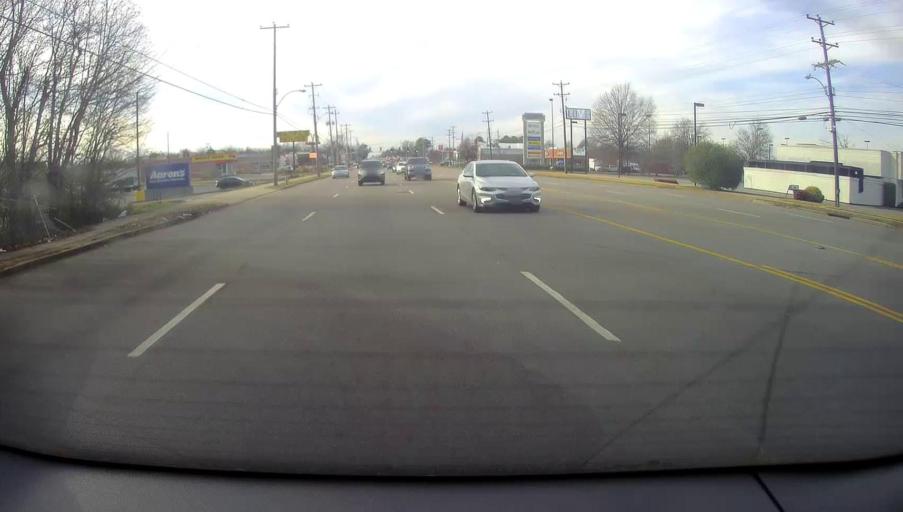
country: US
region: Tennessee
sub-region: Shelby County
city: Germantown
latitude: 35.0489
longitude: -89.8251
